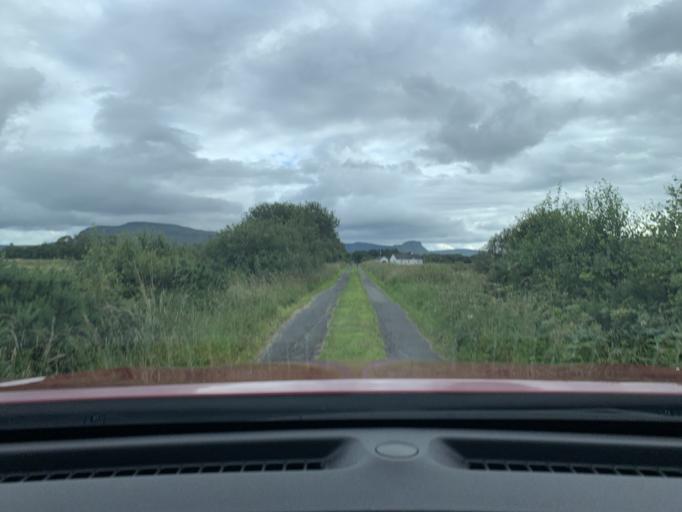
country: IE
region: Connaught
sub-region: County Leitrim
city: Kinlough
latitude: 54.4618
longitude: -8.3539
